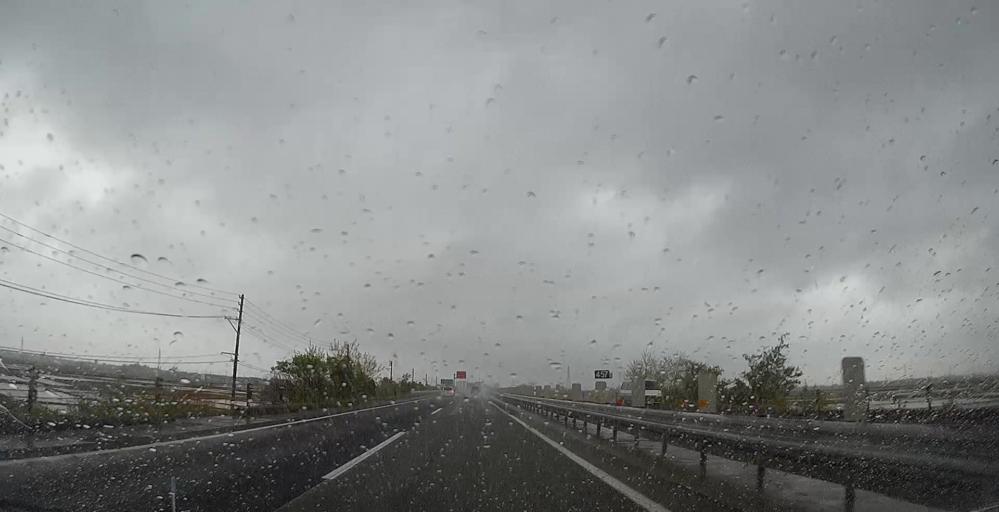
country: JP
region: Niigata
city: Maki
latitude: 37.7379
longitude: 138.9378
